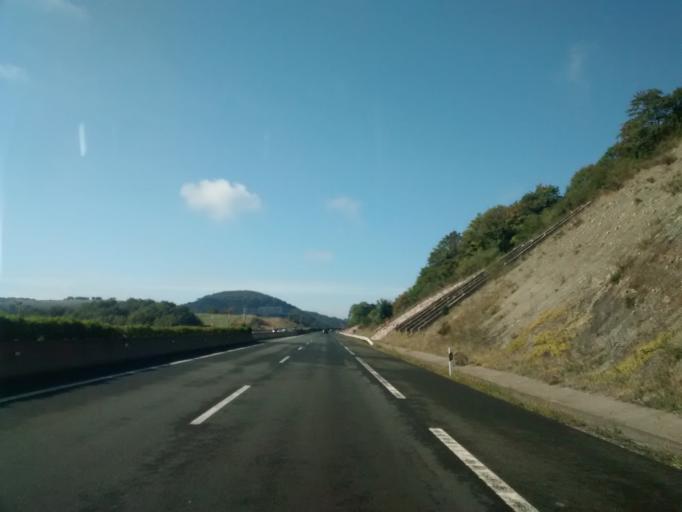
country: ES
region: Cantabria
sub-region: Provincia de Cantabria
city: Santiurde de Reinosa
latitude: 43.0359
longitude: -4.0941
